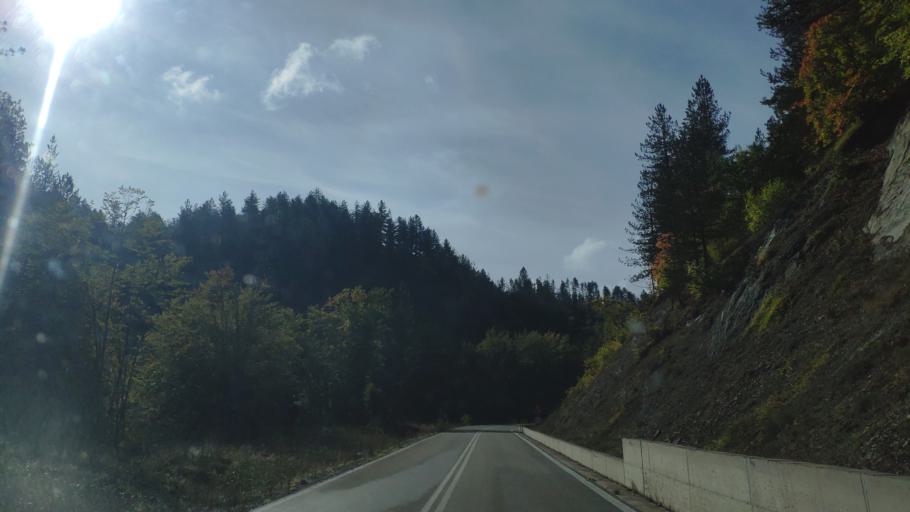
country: GR
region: West Macedonia
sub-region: Nomos Kastorias
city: Nestorio
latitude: 40.3780
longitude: 20.9413
